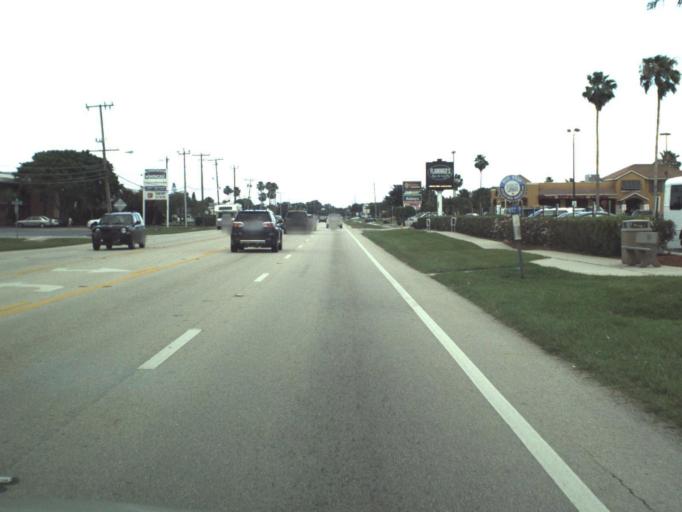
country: US
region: Florida
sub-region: Brevard County
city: Cape Canaveral
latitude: 28.3961
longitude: -80.6121
